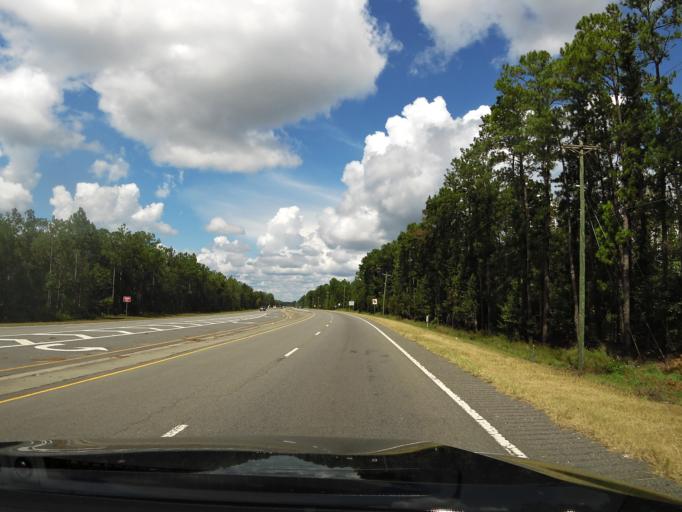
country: US
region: Georgia
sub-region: Charlton County
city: Folkston
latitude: 30.7818
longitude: -81.9791
